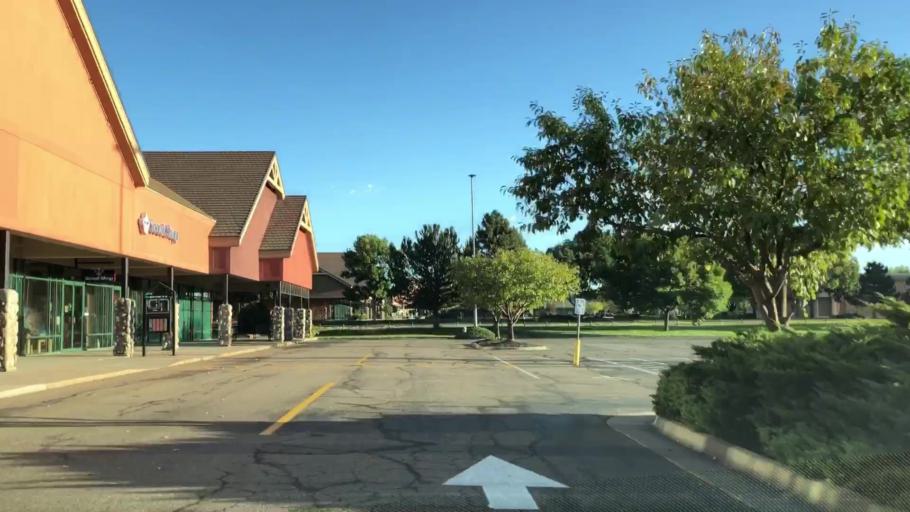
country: US
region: Colorado
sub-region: Larimer County
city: Loveland
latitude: 40.4100
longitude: -104.9967
